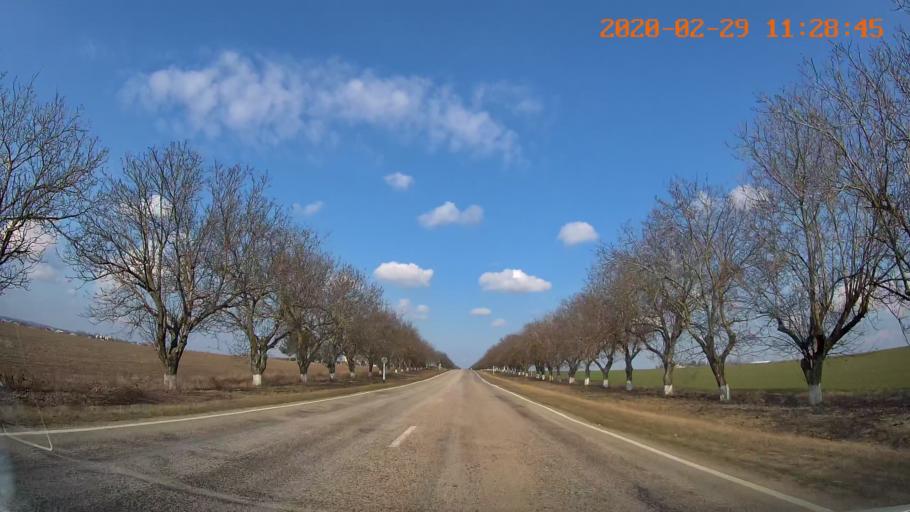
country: MD
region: Telenesti
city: Cocieri
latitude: 47.4839
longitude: 29.1313
